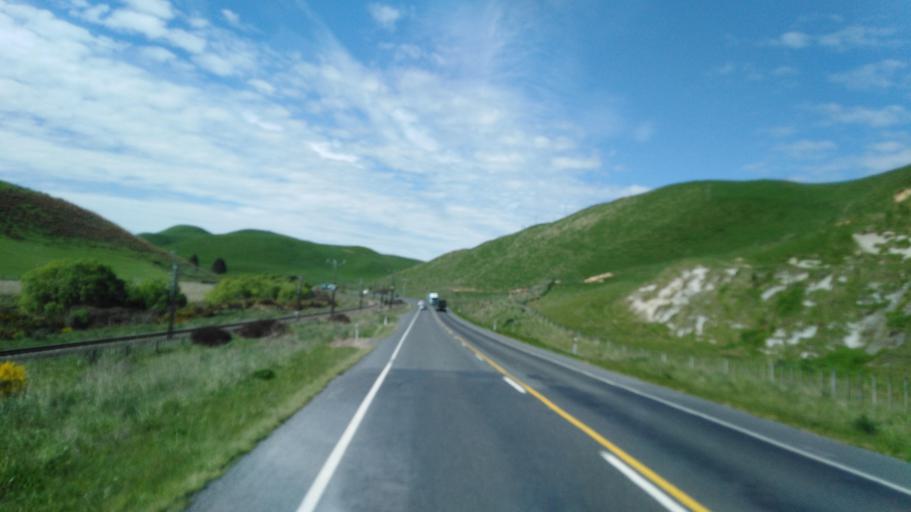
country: NZ
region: Manawatu-Wanganui
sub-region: Ruapehu District
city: Waiouru
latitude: -39.5019
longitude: 175.6738
